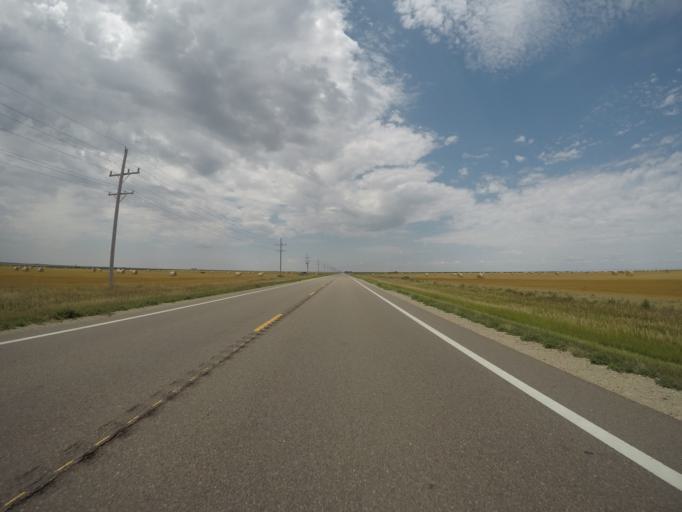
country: US
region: Kansas
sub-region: Thomas County
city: Colby
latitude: 39.3942
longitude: -100.9182
